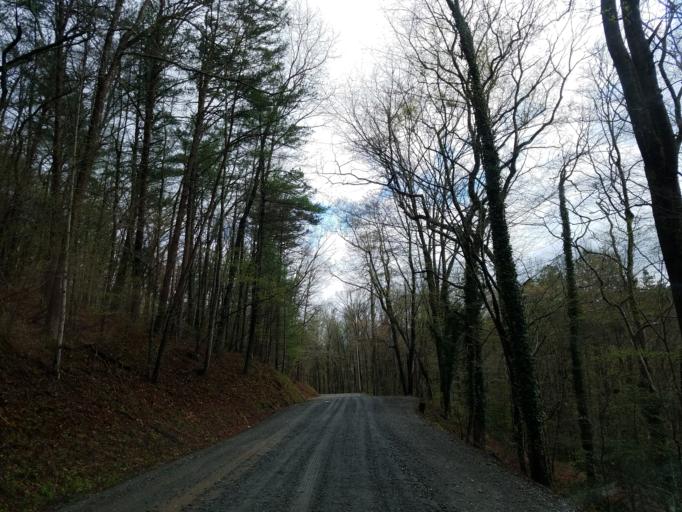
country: US
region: Georgia
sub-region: Fannin County
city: Blue Ridge
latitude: 34.8085
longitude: -84.2455
